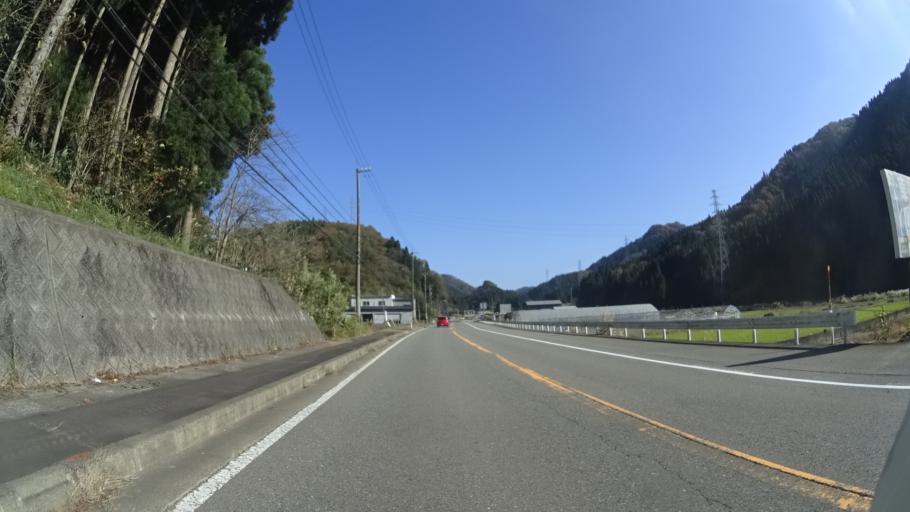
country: JP
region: Fukui
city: Ono
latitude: 35.9990
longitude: 136.4233
